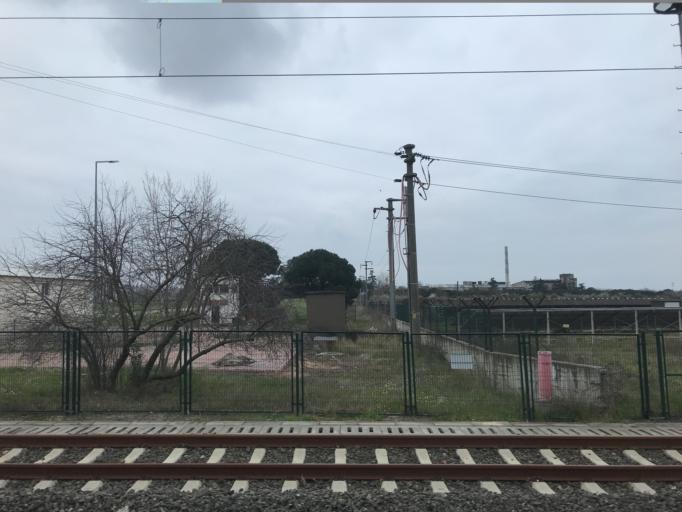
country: TR
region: Kocaeli
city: Darica
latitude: 40.8094
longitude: 29.3543
